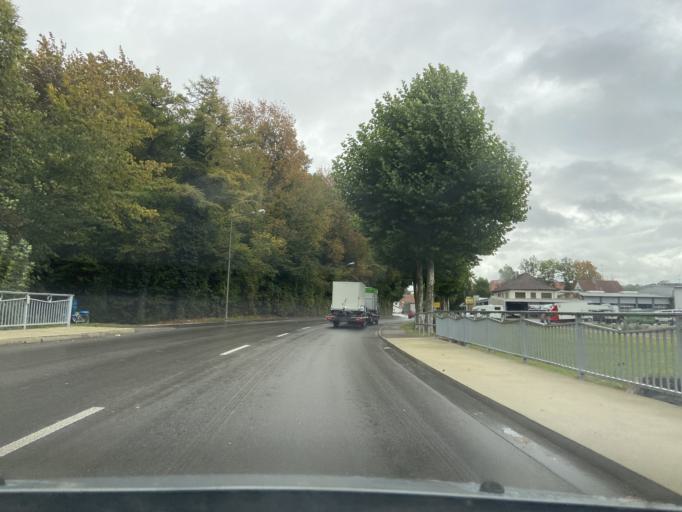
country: DE
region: Baden-Wuerttemberg
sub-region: Tuebingen Region
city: Krauchenwies
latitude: 48.0193
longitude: 9.2438
